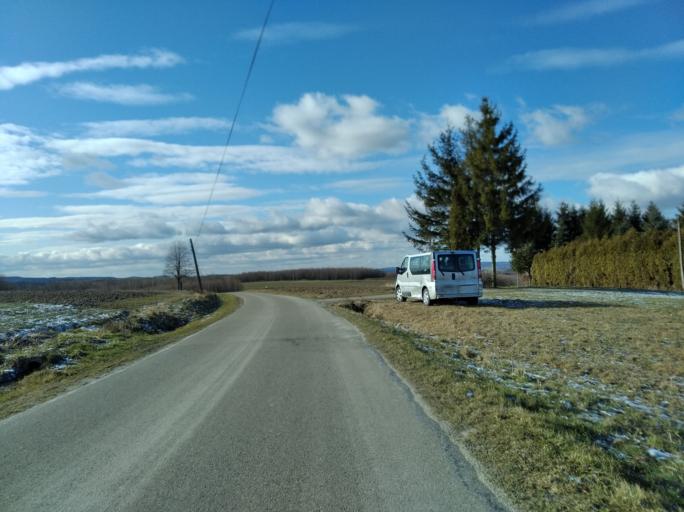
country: PL
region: Subcarpathian Voivodeship
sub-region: Powiat ropczycko-sedziszowski
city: Wielopole Skrzynskie
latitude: 49.9168
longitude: 21.6321
